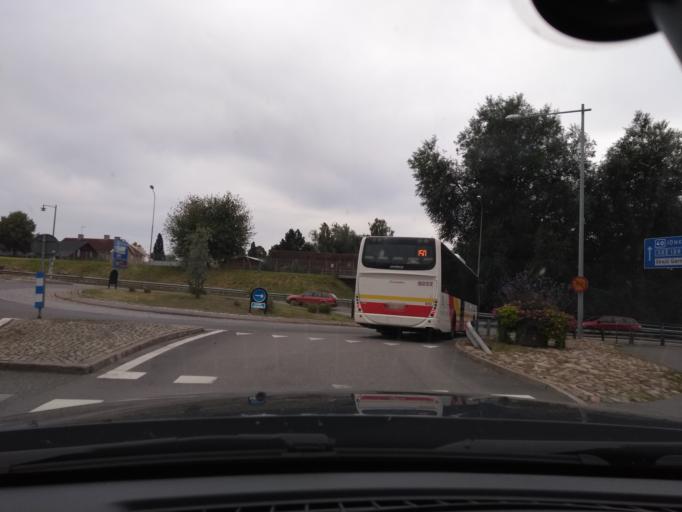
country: SE
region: Joenkoeping
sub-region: Eksjo Kommun
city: Eksjoe
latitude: 57.6640
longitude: 14.9708
